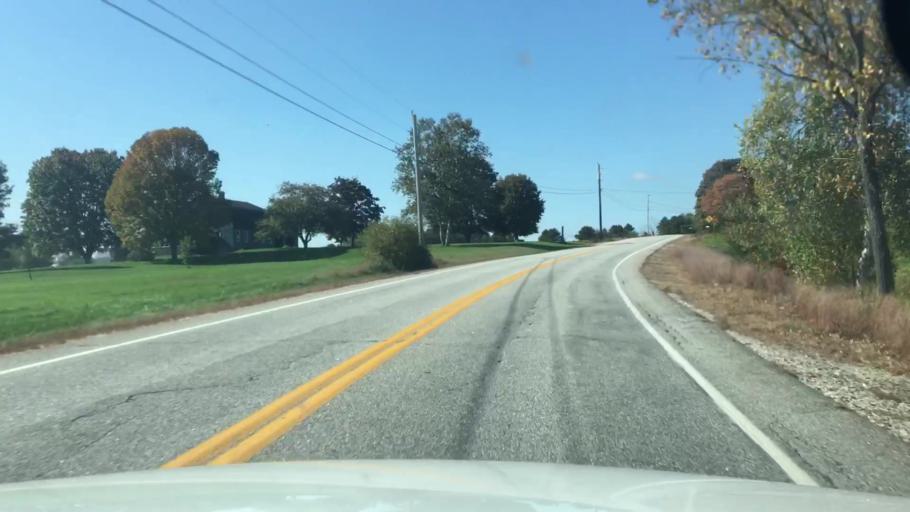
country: US
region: Maine
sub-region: Androscoggin County
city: Lisbon Falls
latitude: 44.0385
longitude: -70.0287
